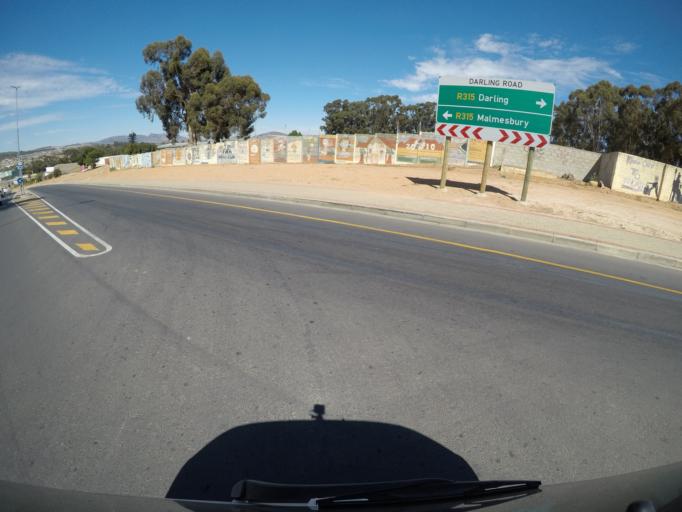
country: ZA
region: Western Cape
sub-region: West Coast District Municipality
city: Malmesbury
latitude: -33.4637
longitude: 18.7139
